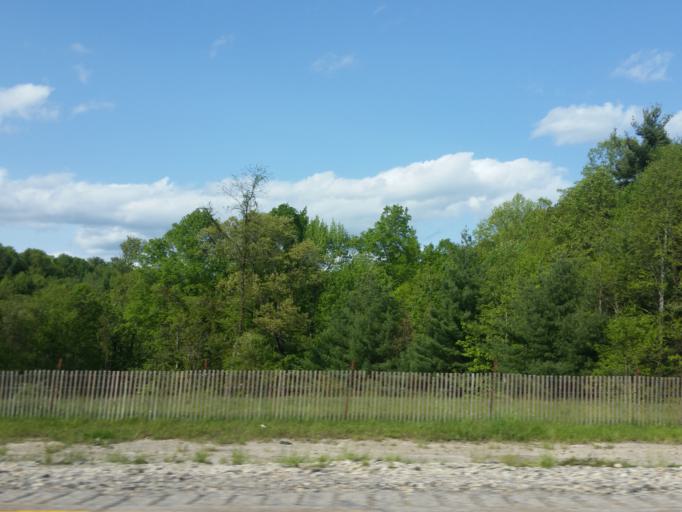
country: US
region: West Virginia
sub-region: Raleigh County
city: MacArthur
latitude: 37.7243
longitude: -81.1868
